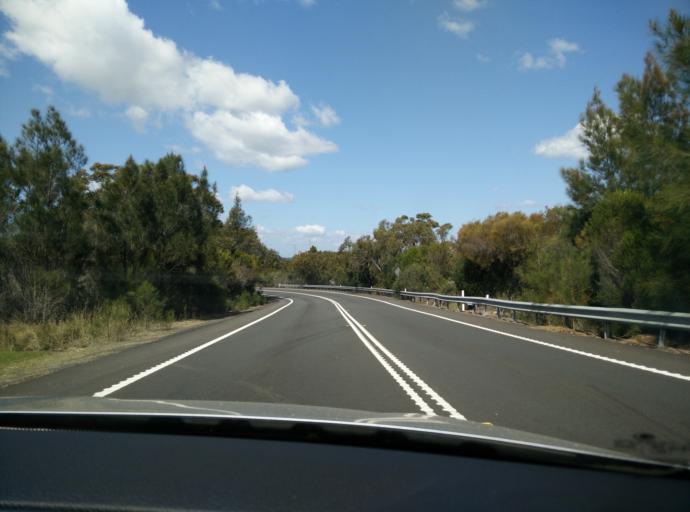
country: AU
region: New South Wales
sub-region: Gosford Shire
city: Blackwall
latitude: -33.4722
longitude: 151.2880
